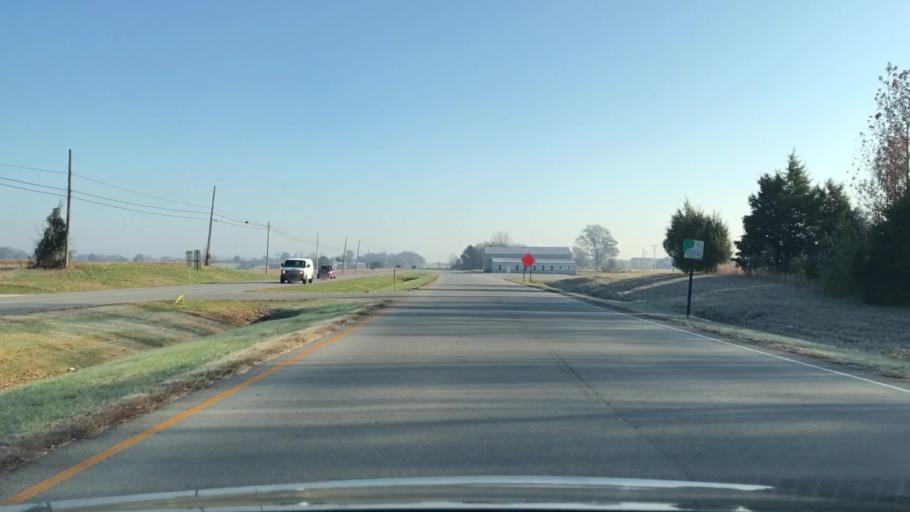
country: US
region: Kentucky
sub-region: Warren County
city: Bowling Green
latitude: 37.0397
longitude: -86.3317
